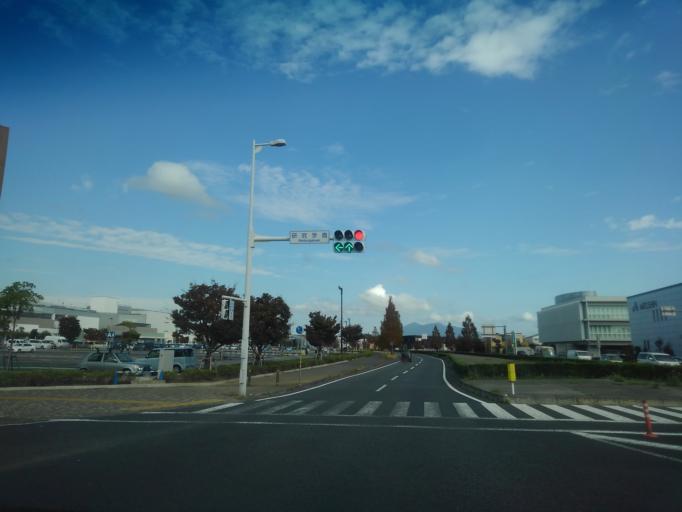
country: JP
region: Ibaraki
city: Naka
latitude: 36.0844
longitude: 140.0864
